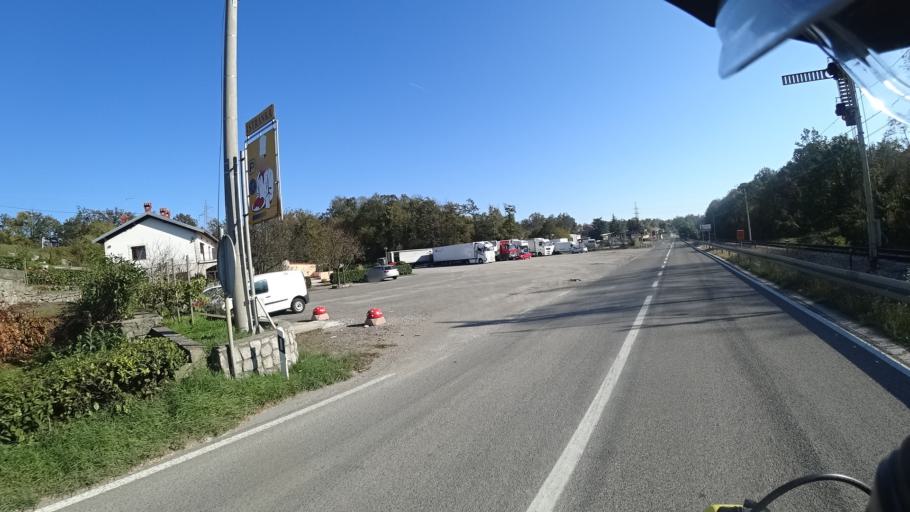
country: HR
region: Primorsko-Goranska
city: Matulji
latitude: 45.3876
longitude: 14.3120
